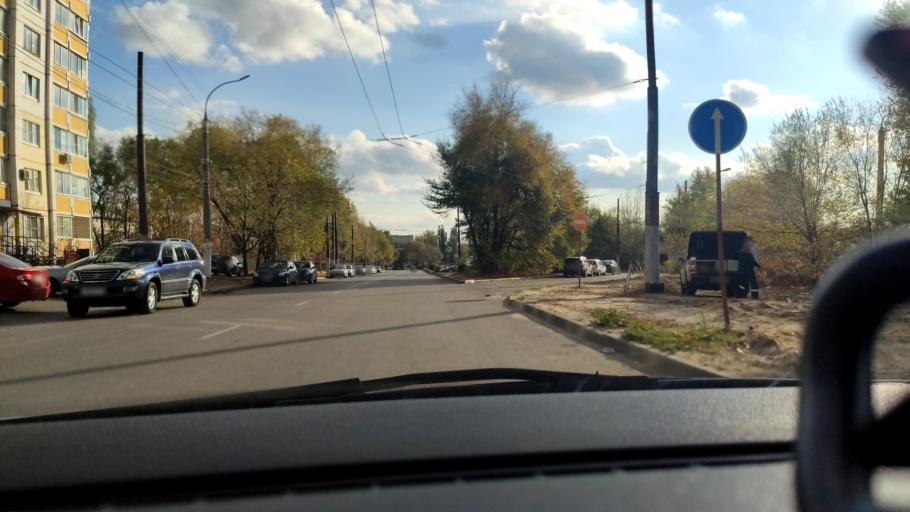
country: RU
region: Voronezj
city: Pridonskoy
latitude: 51.6519
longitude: 39.1007
